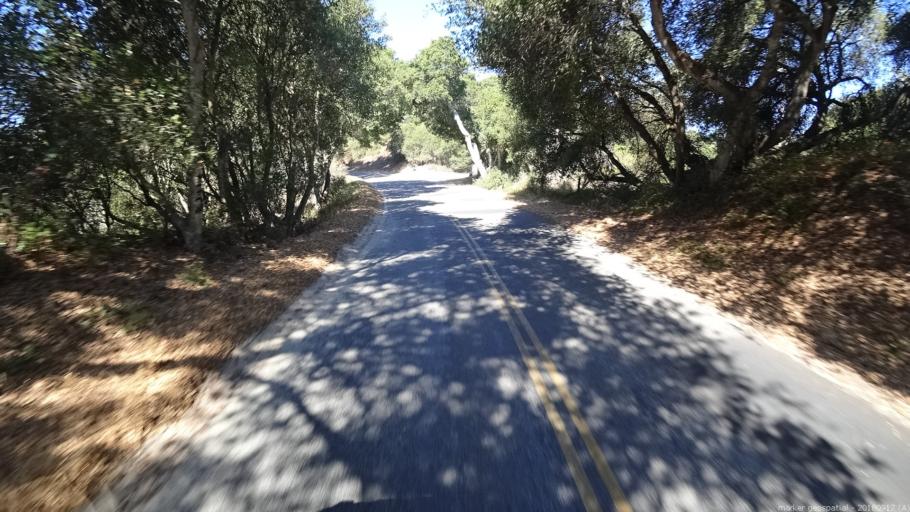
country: US
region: California
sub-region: Monterey County
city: Elkhorn
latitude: 36.8307
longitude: -121.7314
